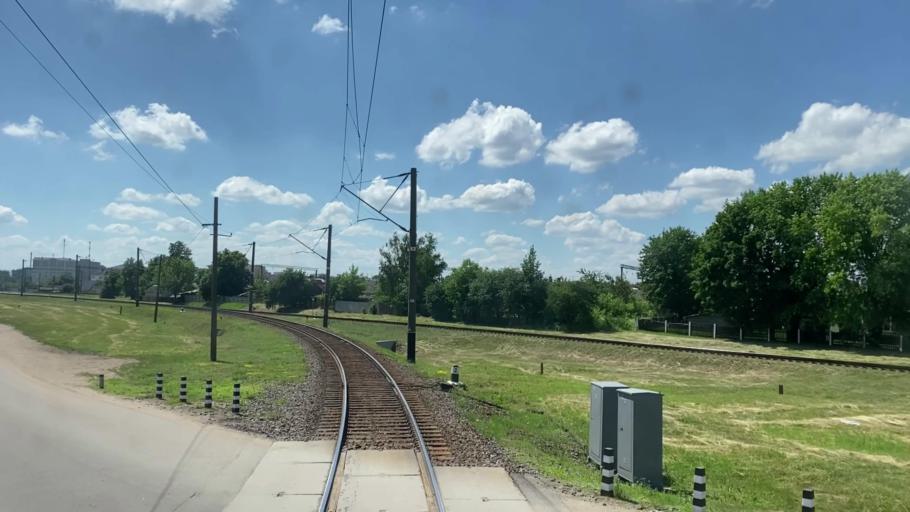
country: BY
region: Brest
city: Baranovichi
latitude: 53.1398
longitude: 26.0319
